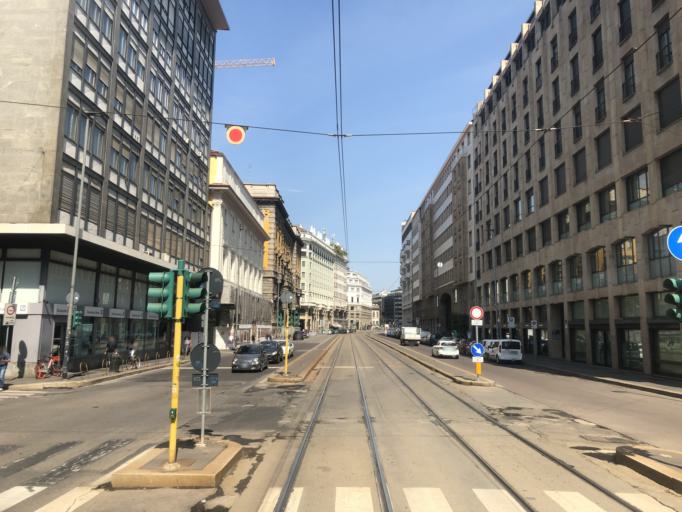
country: IT
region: Lombardy
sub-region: Citta metropolitana di Milano
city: Milano
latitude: 45.4609
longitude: 9.1914
